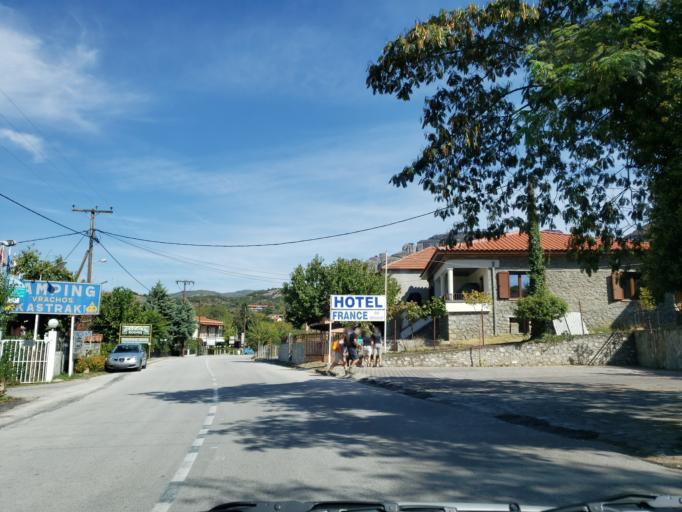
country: GR
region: Thessaly
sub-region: Trikala
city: Kastraki
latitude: 39.7131
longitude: 21.6160
